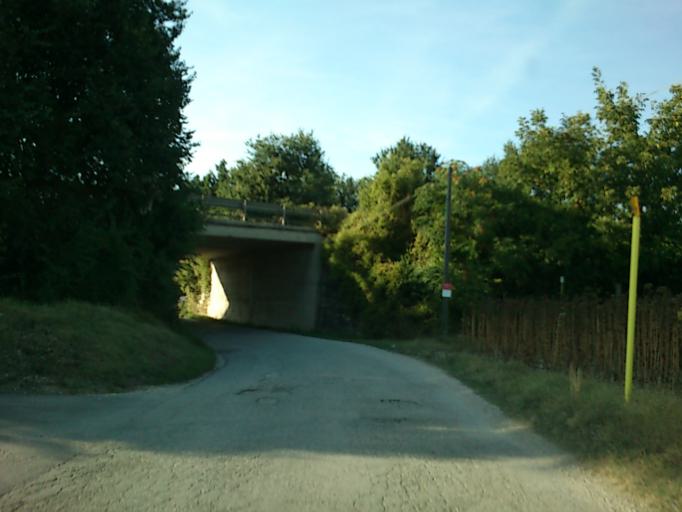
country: IT
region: The Marches
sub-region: Provincia di Pesaro e Urbino
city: Saltara
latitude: 43.7384
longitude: 12.9079
